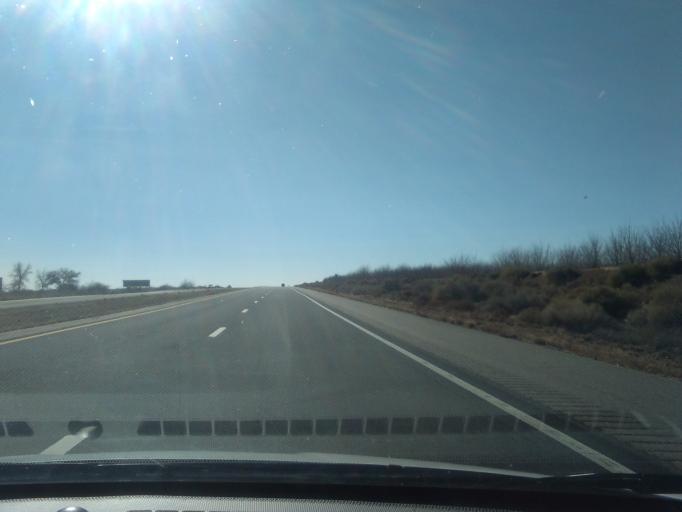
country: US
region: New Mexico
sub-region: Valencia County
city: Jarales
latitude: 34.6002
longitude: -106.7879
